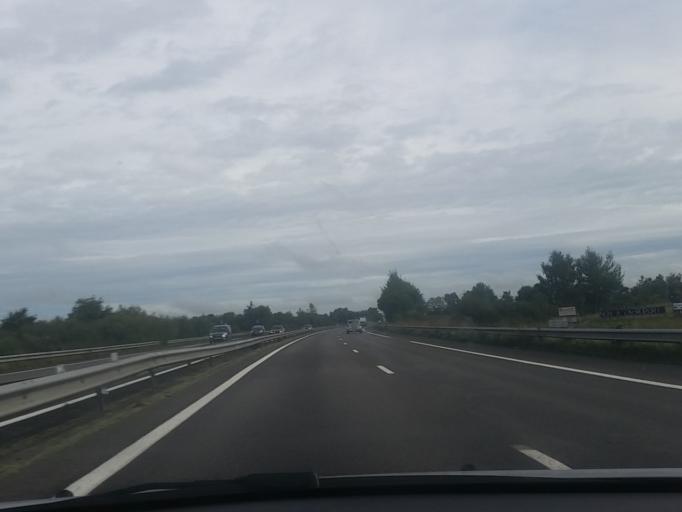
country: FR
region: Pays de la Loire
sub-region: Departement de la Loire-Atlantique
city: Treillieres
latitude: 47.3644
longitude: -1.6539
